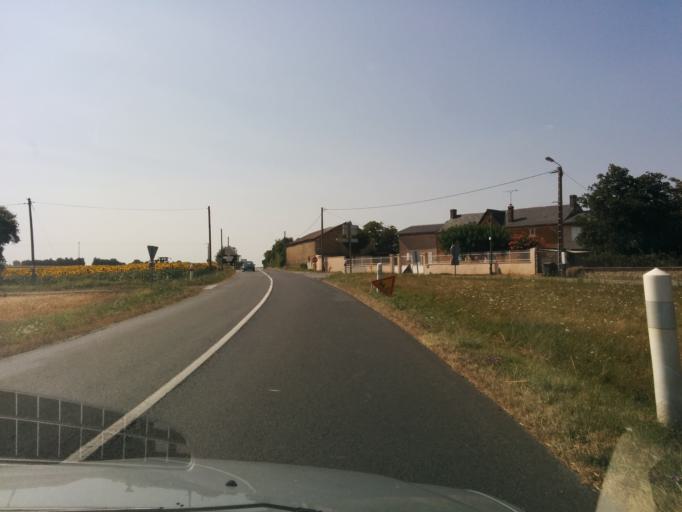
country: FR
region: Poitou-Charentes
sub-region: Departement de la Vienne
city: Saint-Jean-de-Sauves
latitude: 46.7942
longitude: 0.1129
